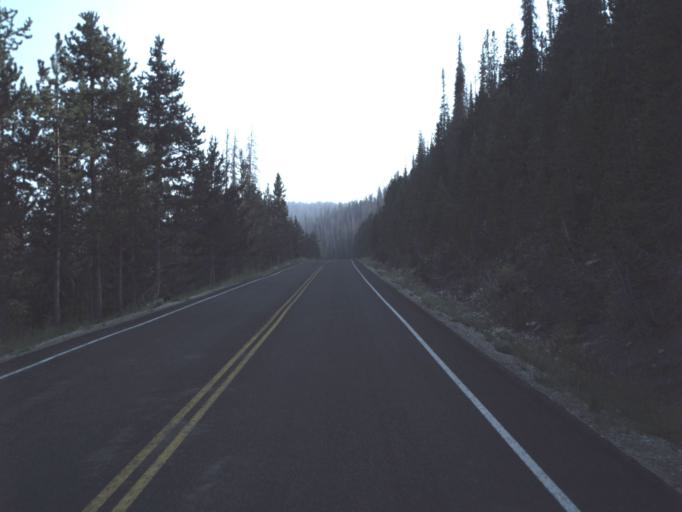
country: US
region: Utah
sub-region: Summit County
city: Kamas
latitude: 40.7673
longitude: -110.8830
